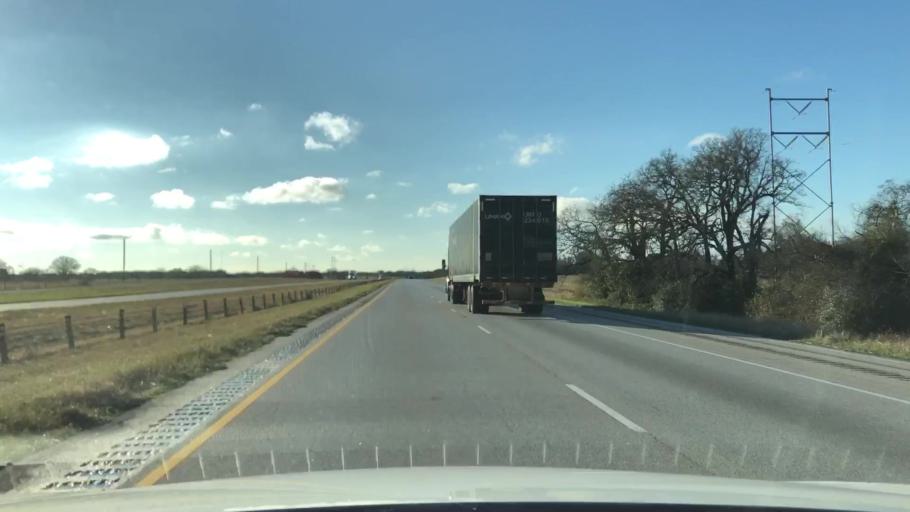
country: US
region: Texas
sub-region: Colorado County
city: Weimar
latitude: 29.6892
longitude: -96.6893
